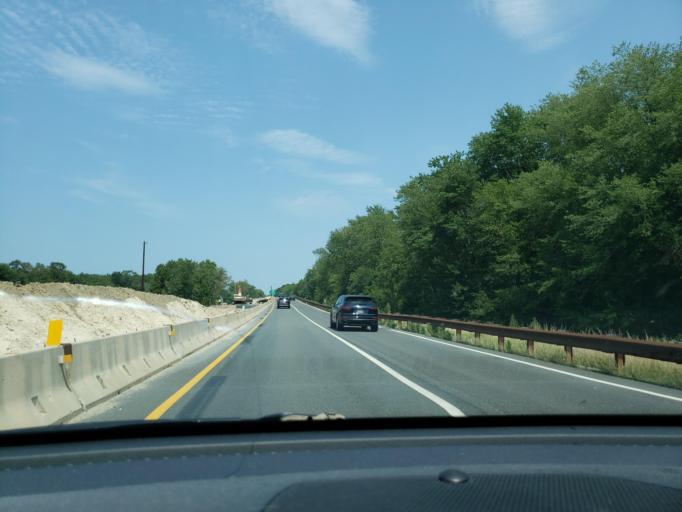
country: US
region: New Jersey
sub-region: Atlantic County
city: Northfield
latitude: 39.3773
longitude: -74.5803
